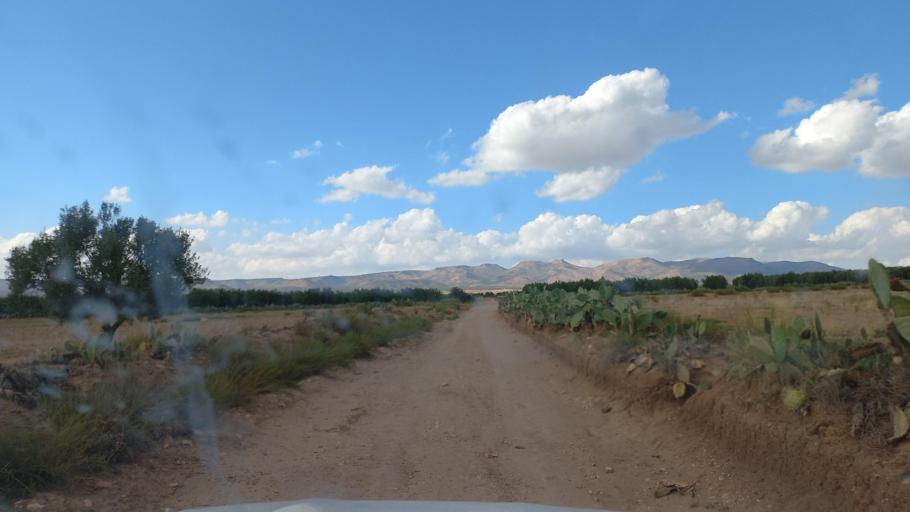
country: TN
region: Al Qasrayn
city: Sbiba
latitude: 35.3901
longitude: 9.0392
